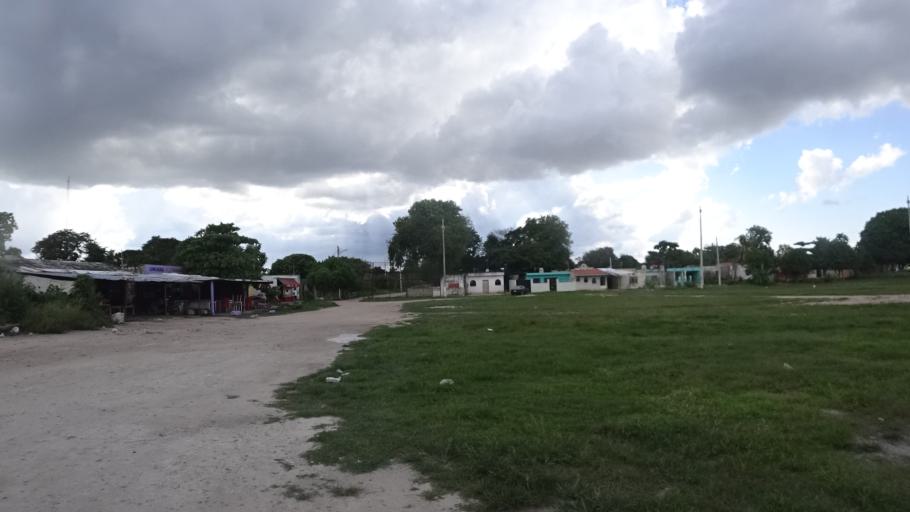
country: MX
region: Yucatan
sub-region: Kanasin
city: Kanasin
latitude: 20.9495
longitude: -89.5539
